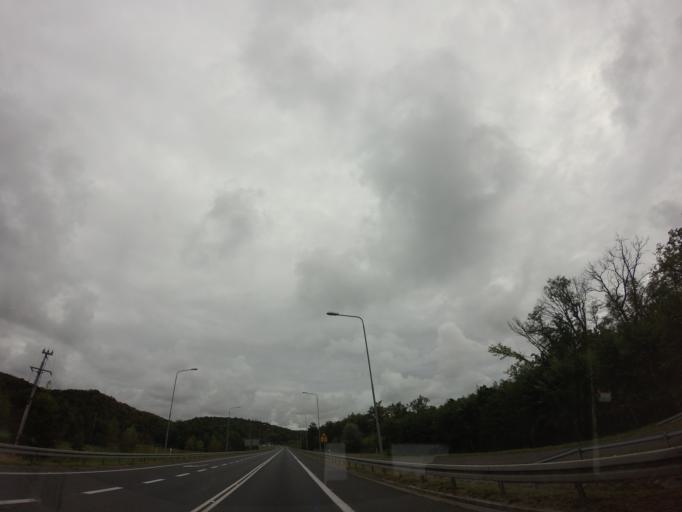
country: PL
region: West Pomeranian Voivodeship
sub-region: Powiat kamienski
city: Miedzyzdroje
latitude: 53.9106
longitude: 14.4303
